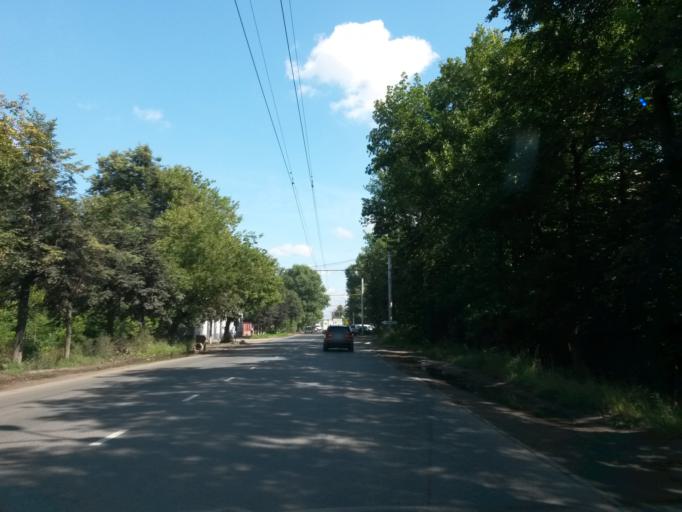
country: RU
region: Ivanovo
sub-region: Gorod Ivanovo
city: Ivanovo
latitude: 57.0052
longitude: 40.9476
